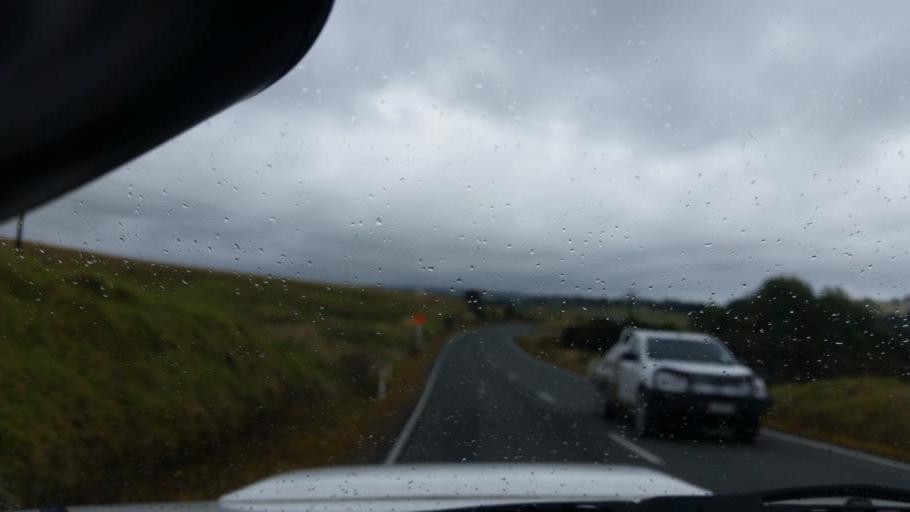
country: NZ
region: Auckland
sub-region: Auckland
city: Wellsford
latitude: -36.1436
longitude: 174.4983
